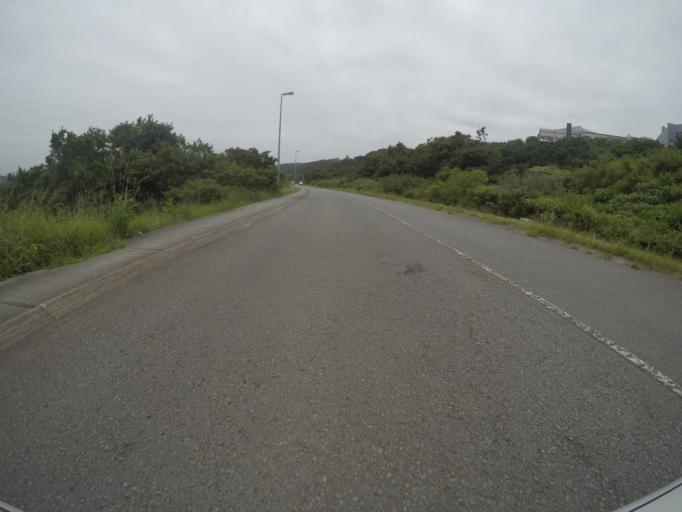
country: ZA
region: Eastern Cape
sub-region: Buffalo City Metropolitan Municipality
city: East London
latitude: -32.9795
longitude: 27.9333
